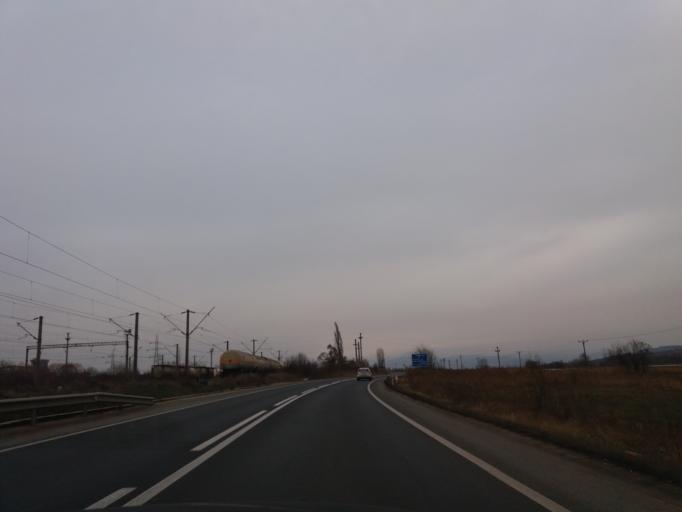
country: RO
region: Hunedoara
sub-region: Comuna Calan
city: Calan
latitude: 45.7558
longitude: 23.0007
